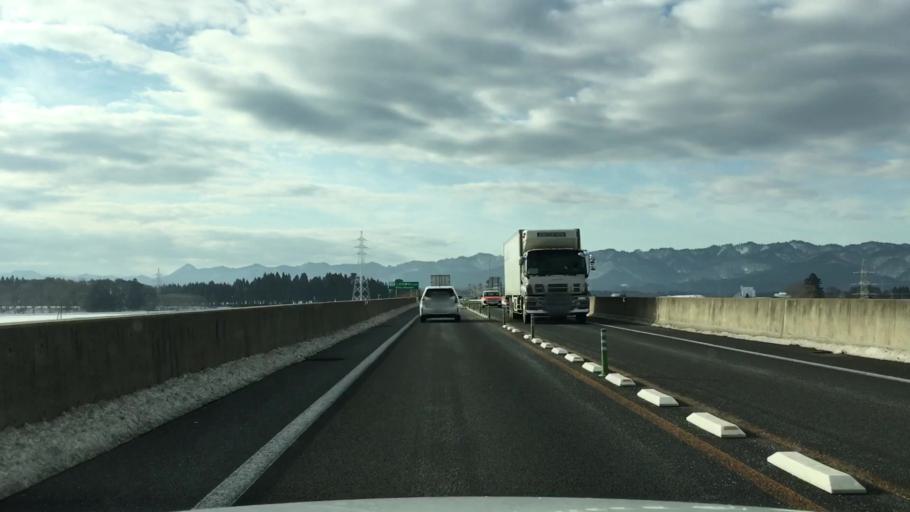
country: JP
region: Akita
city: Odate
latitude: 40.2649
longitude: 140.5259
